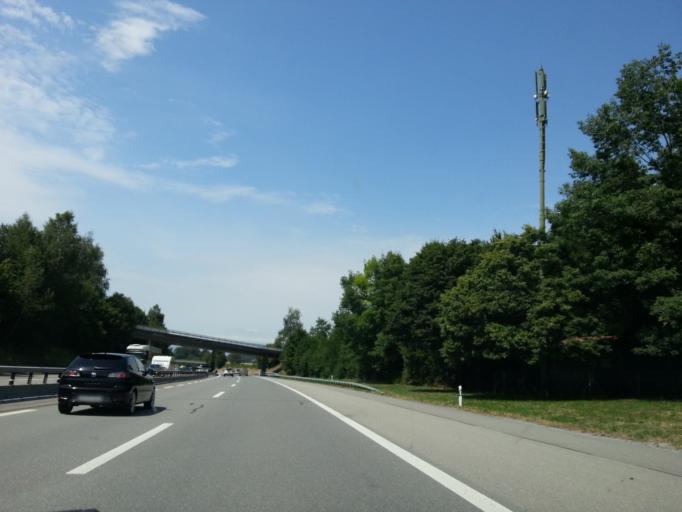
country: CH
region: Bern
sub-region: Bern-Mittelland District
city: Muhleberg
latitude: 46.9577
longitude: 7.2986
